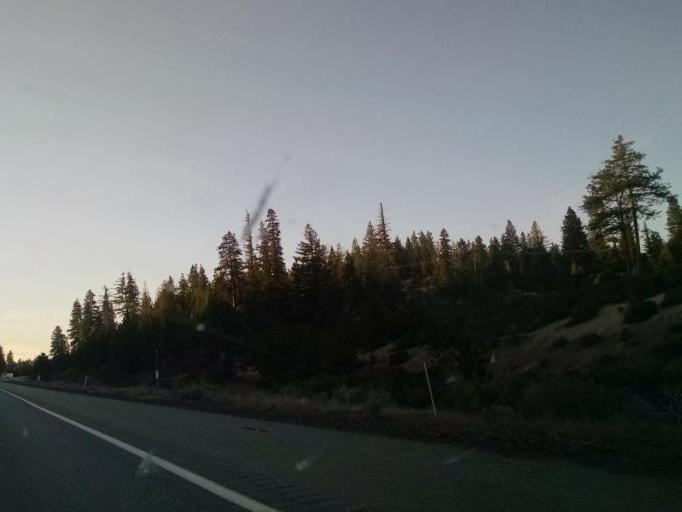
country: US
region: California
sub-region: Siskiyou County
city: Weed
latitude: 41.3694
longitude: -122.3711
